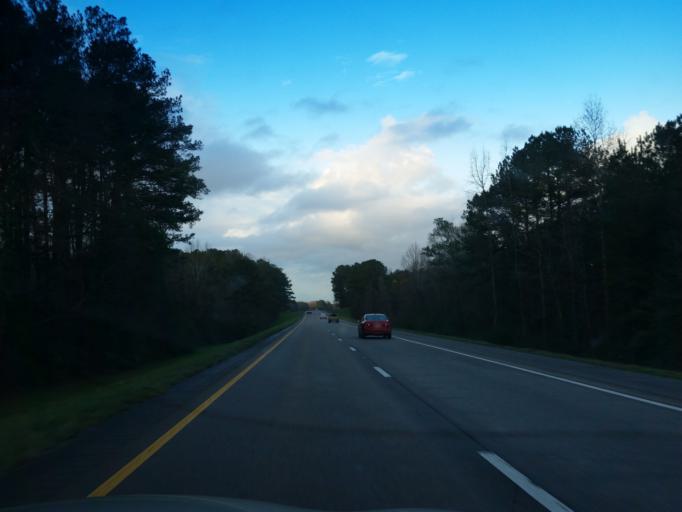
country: US
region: Mississippi
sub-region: Clarke County
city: Stonewall
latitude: 31.9840
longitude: -88.9495
